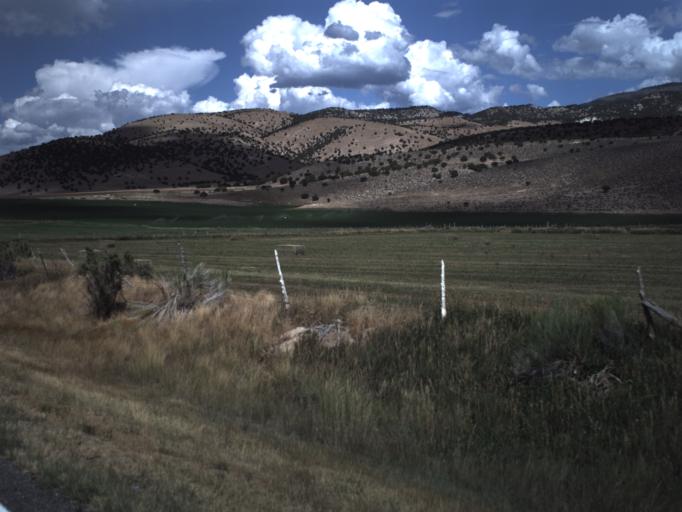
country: US
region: Utah
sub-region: Sanpete County
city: Gunnison
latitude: 39.1580
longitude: -111.7080
